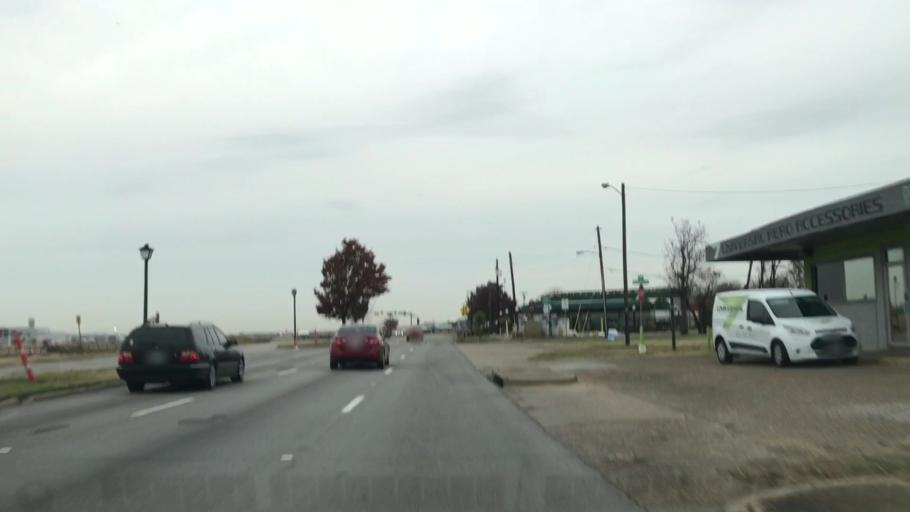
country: US
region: Texas
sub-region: Dallas County
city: University Park
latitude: 32.8380
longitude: -96.8329
